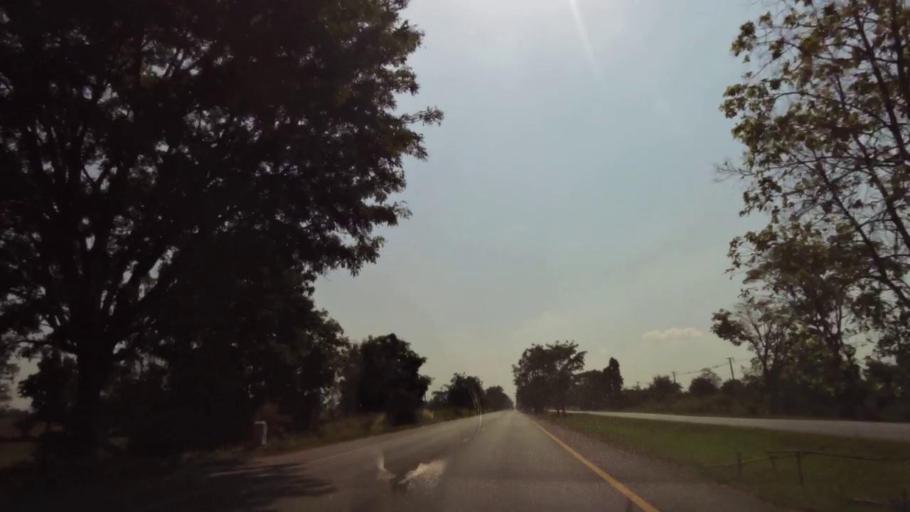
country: TH
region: Phichit
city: Bueng Na Rang
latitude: 16.2886
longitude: 100.1278
